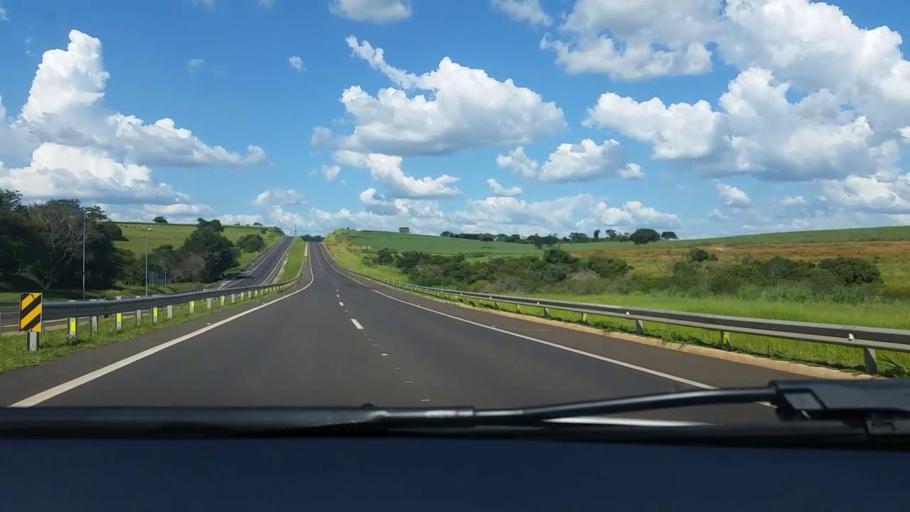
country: BR
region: Sao Paulo
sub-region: Bauru
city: Bauru
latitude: -22.4408
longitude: -49.1471
